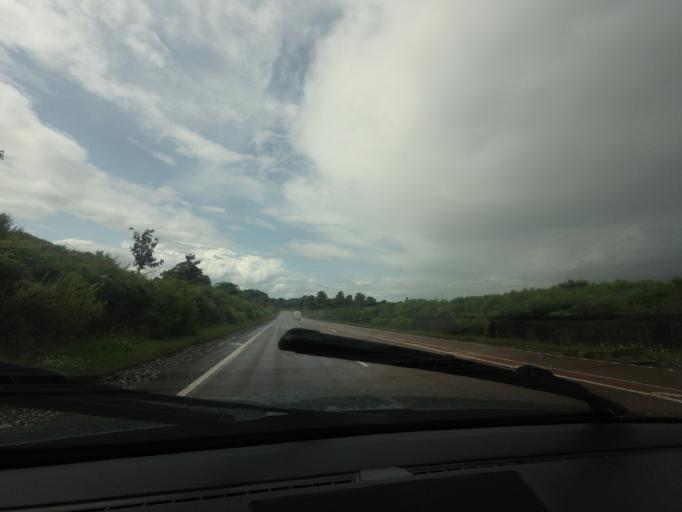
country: GB
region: Scotland
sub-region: Moray
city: Fochabers
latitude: 57.6140
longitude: -3.0905
